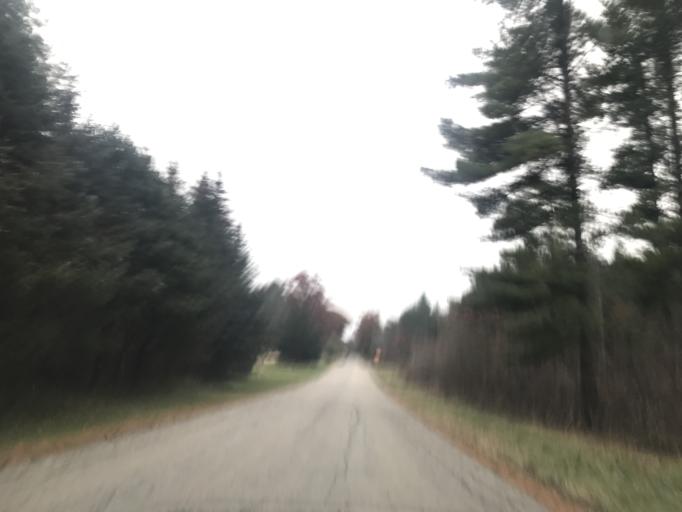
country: US
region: Wisconsin
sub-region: Marinette County
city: Peshtigo
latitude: 45.1091
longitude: -87.7500
